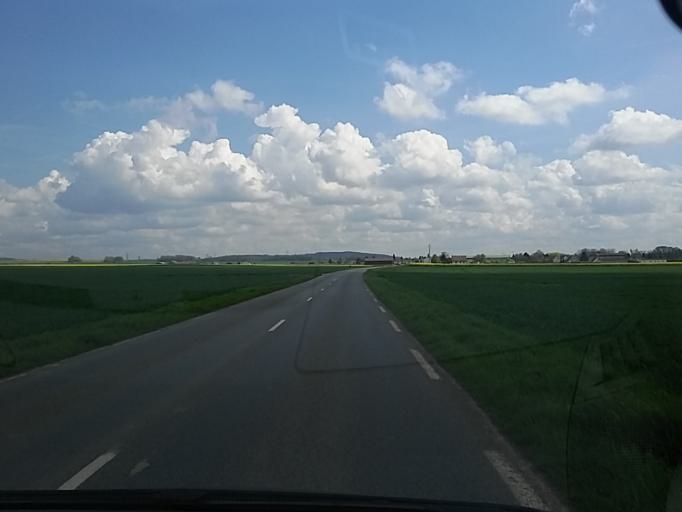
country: FR
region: Picardie
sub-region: Departement de l'Oise
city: Chevrieres
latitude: 49.3463
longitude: 2.6594
